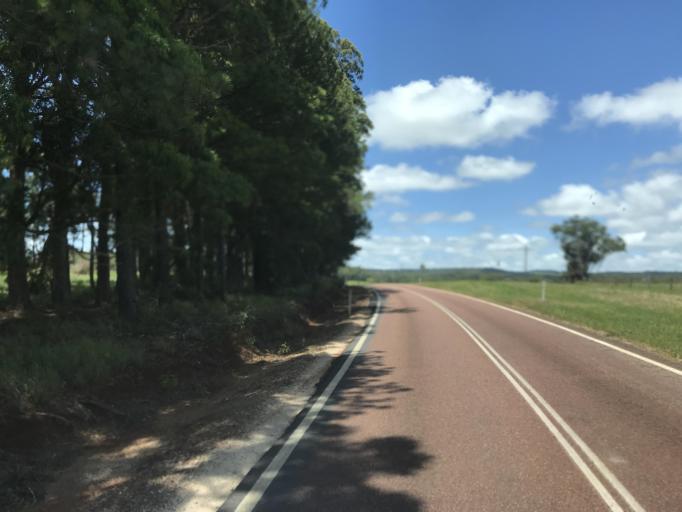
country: AU
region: Queensland
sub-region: Tablelands
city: Ravenshoe
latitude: -17.5295
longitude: 145.4539
